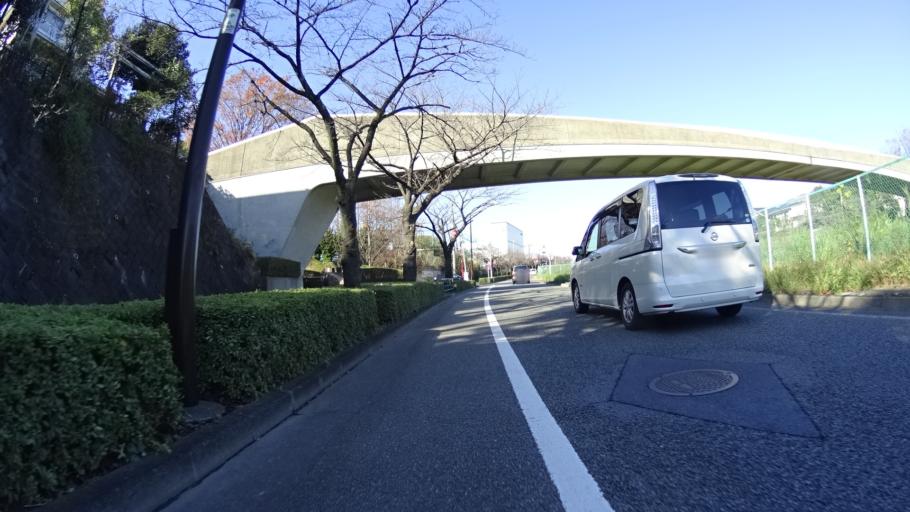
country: JP
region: Tokyo
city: Hino
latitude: 35.6083
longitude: 139.4235
